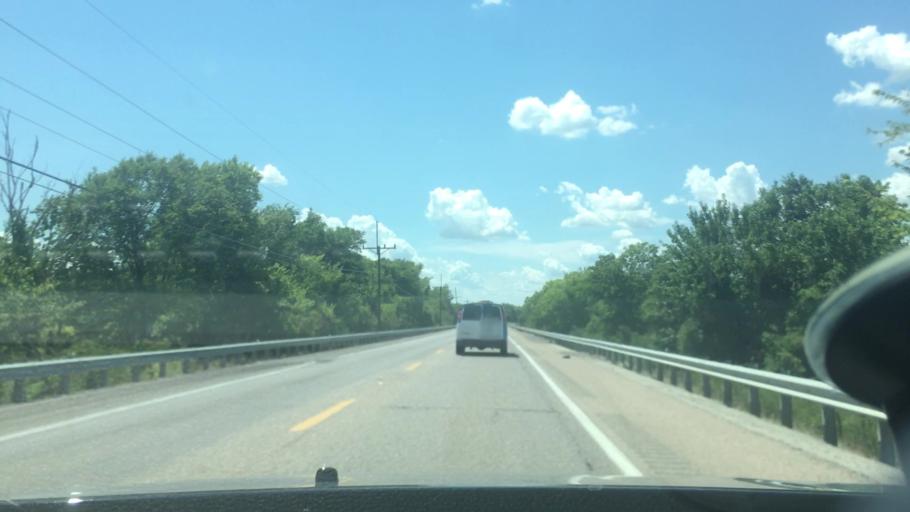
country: US
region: Texas
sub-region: Grayson County
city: Preston
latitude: 33.9983
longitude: -96.5783
